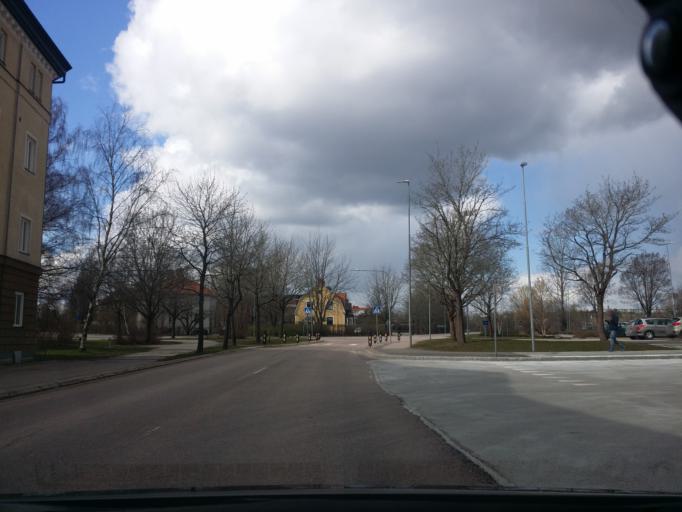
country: SE
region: Vaestmanland
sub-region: Sala Kommun
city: Sala
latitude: 59.9248
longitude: 16.6048
